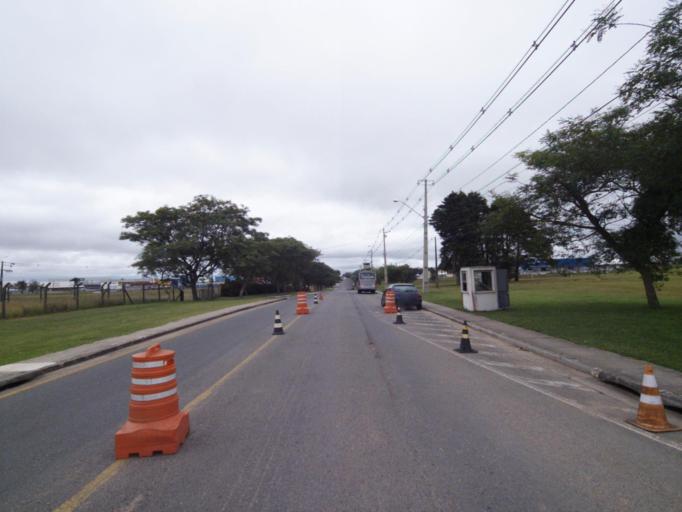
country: BR
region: Parana
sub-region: Sao Jose Dos Pinhais
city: Sao Jose dos Pinhais
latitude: -25.5354
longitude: -49.1800
